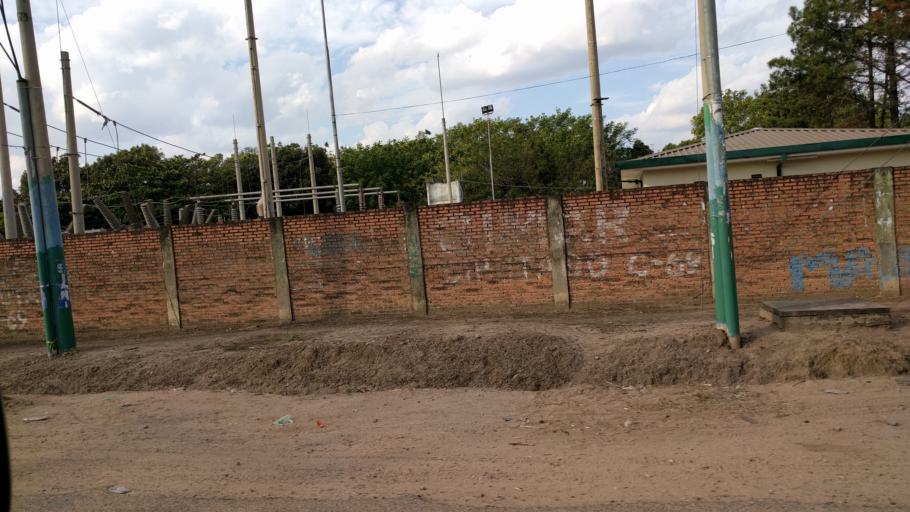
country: BO
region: Santa Cruz
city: Warnes
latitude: -17.5181
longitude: -63.1641
